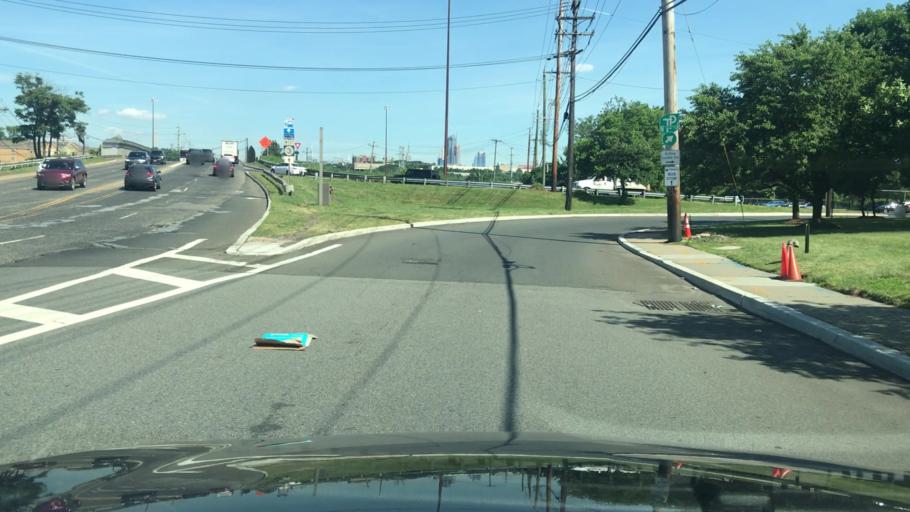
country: US
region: New Jersey
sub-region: Hudson County
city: Secaucus
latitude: 40.7842
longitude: -74.0493
